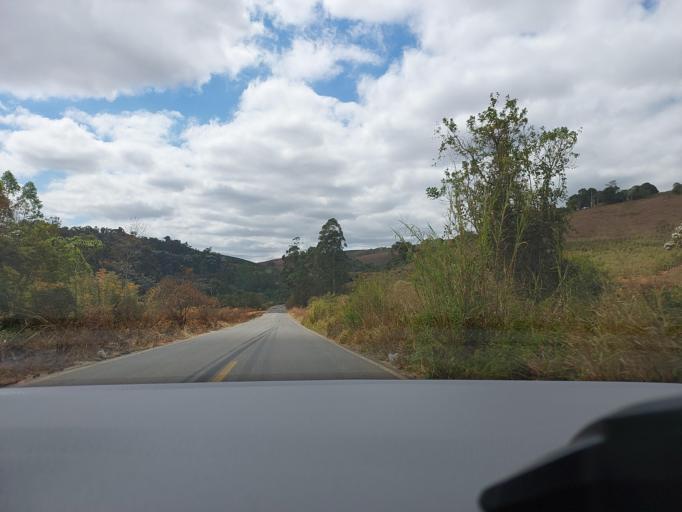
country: BR
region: Minas Gerais
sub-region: Vicosa
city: Vicosa
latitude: -20.8374
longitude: -42.6963
